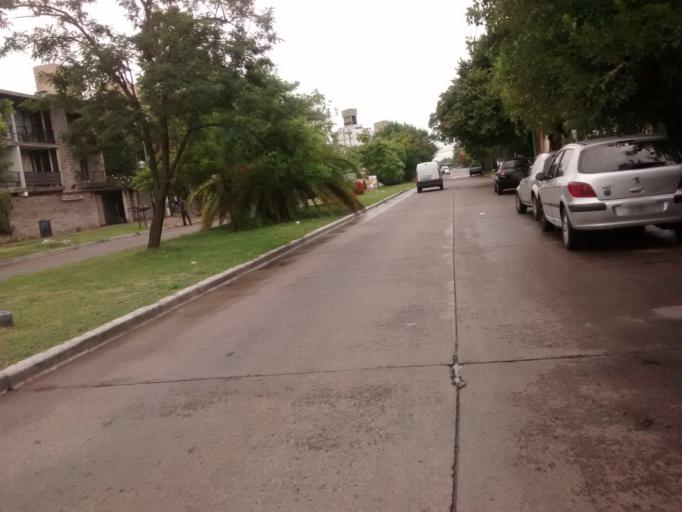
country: AR
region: Buenos Aires
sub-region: Partido de La Plata
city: La Plata
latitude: -34.9001
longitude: -57.9807
